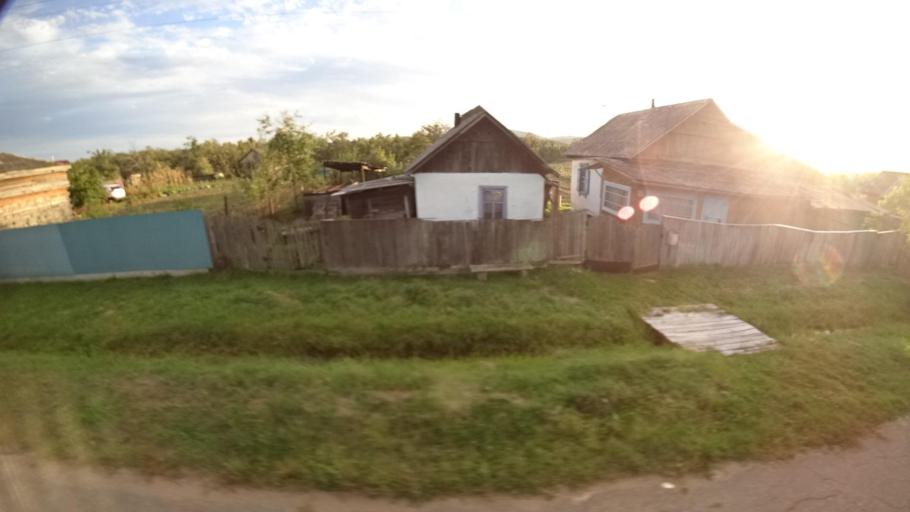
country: RU
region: Primorskiy
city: Yakovlevka
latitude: 44.4239
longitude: 133.4873
